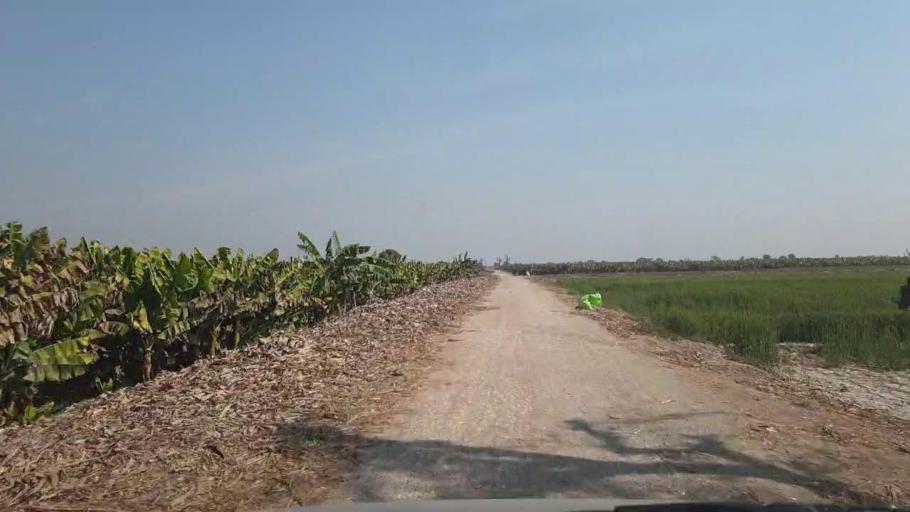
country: PK
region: Sindh
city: Chambar
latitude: 25.3624
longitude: 68.8128
